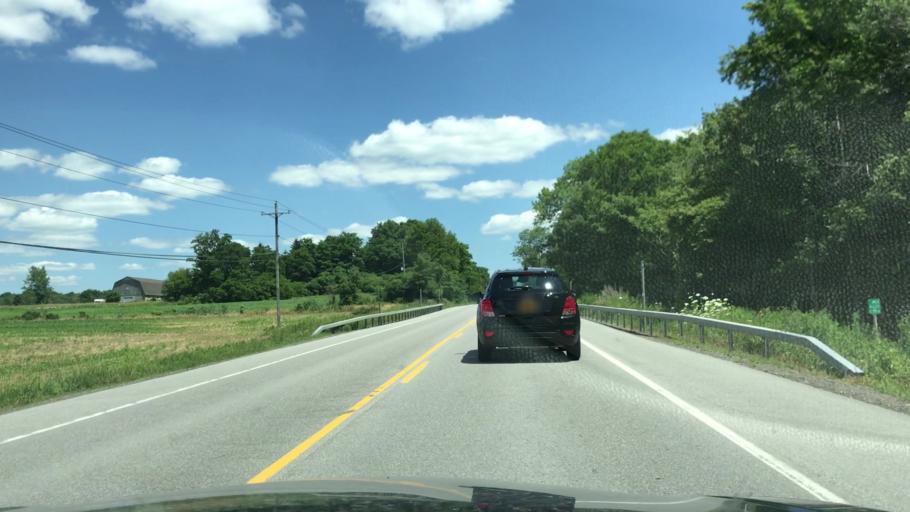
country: US
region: New York
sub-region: Wyoming County
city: Attica
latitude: 42.7705
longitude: -78.3593
